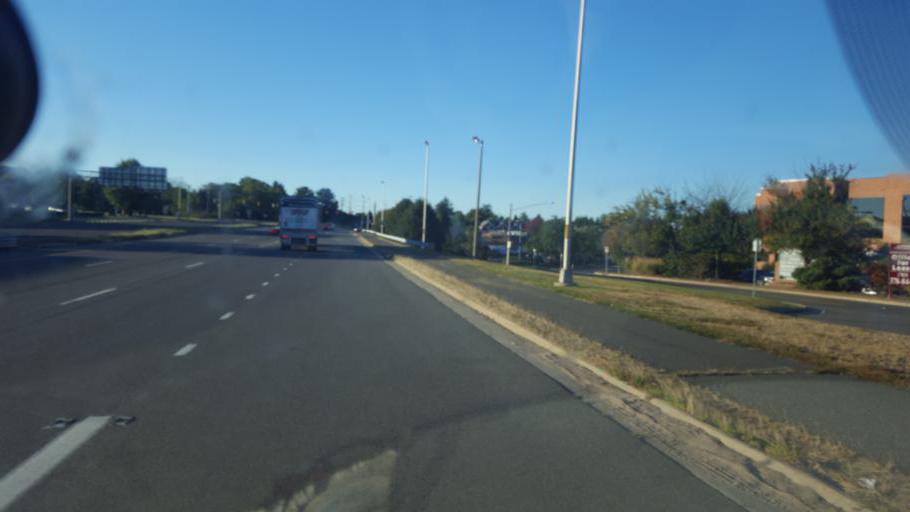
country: US
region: Virginia
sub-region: Fairfax County
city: Centreville
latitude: 38.8361
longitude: -77.4323
